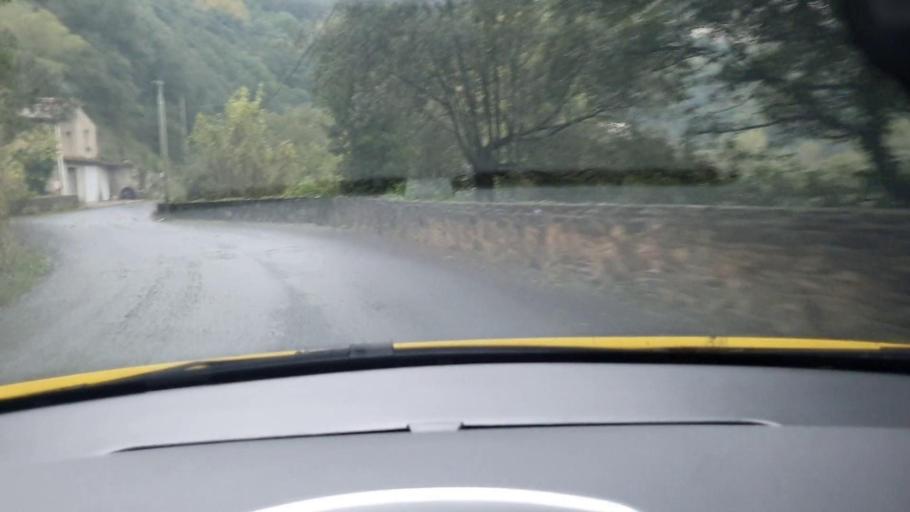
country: FR
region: Languedoc-Roussillon
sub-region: Departement du Gard
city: Sumene
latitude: 44.0044
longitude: 3.7107
